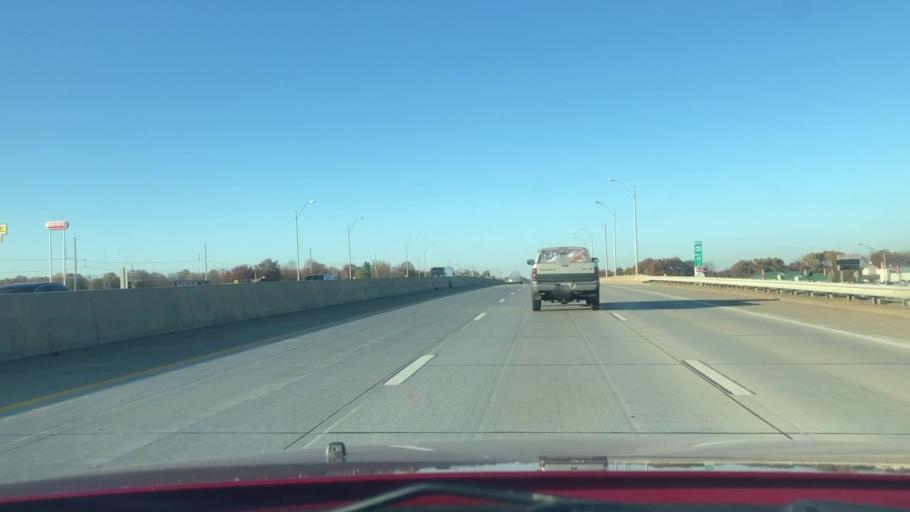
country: US
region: Missouri
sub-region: Greene County
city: Springfield
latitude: 37.1792
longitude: -93.2244
